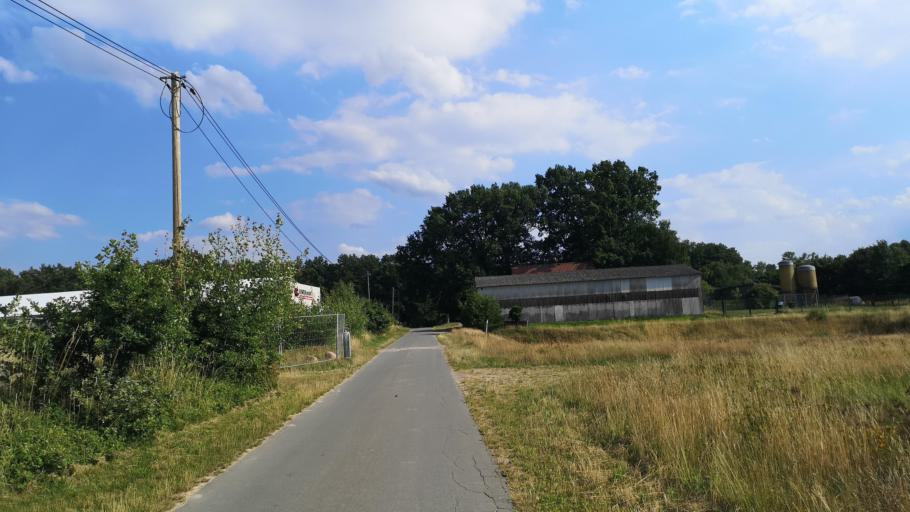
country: DE
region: Lower Saxony
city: Dahlenburg
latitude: 53.2179
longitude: 10.7126
